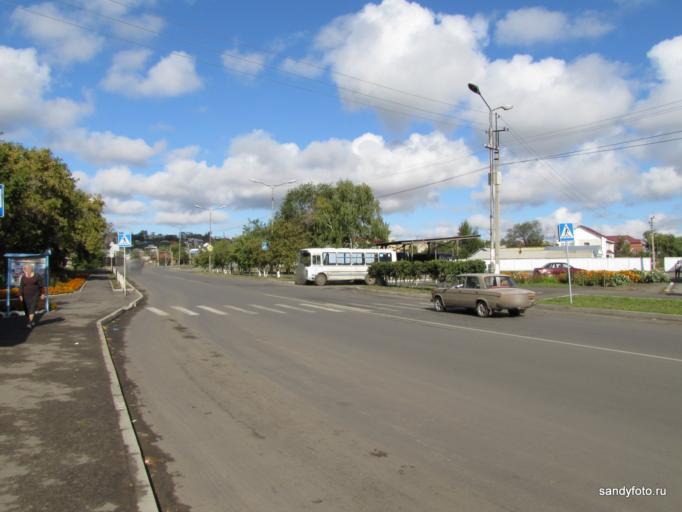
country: RU
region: Chelyabinsk
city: Troitsk
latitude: 54.0952
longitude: 61.5664
